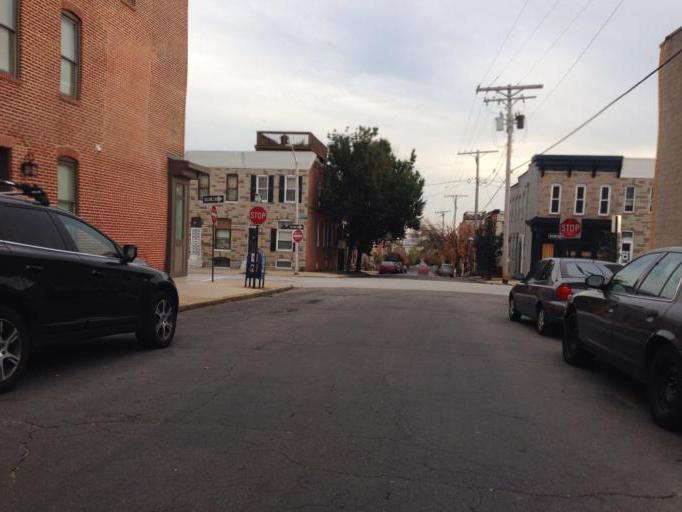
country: US
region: Maryland
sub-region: City of Baltimore
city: Baltimore
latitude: 39.2837
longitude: -76.5706
